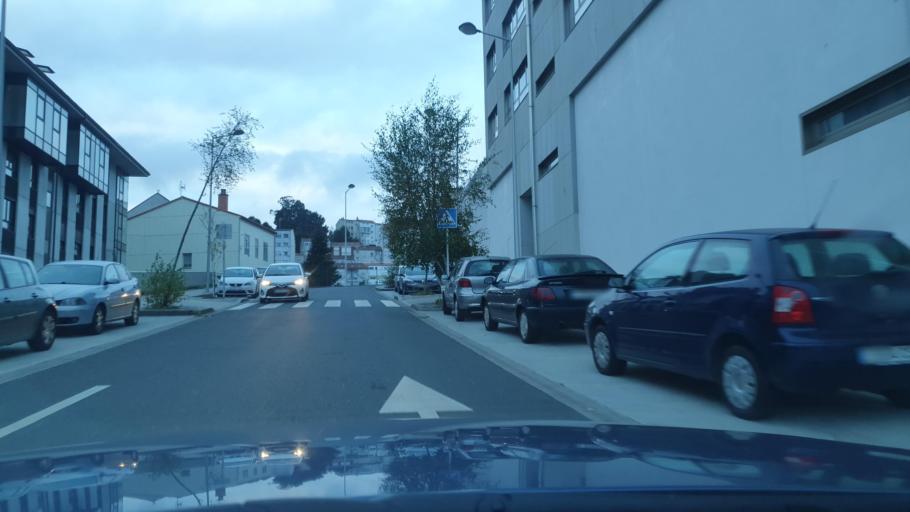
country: ES
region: Galicia
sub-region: Provincia da Coruna
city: Santiago de Compostela
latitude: 42.8843
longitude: -8.5313
